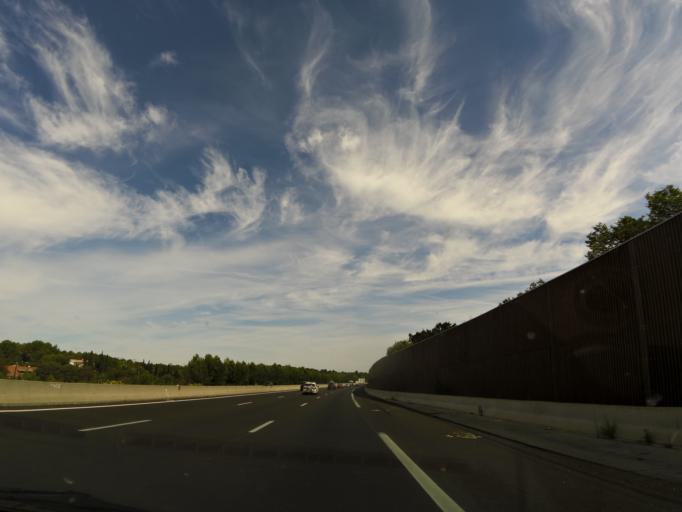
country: FR
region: Languedoc-Roussillon
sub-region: Departement du Gard
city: Uchaud
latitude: 43.7676
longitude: 4.2700
